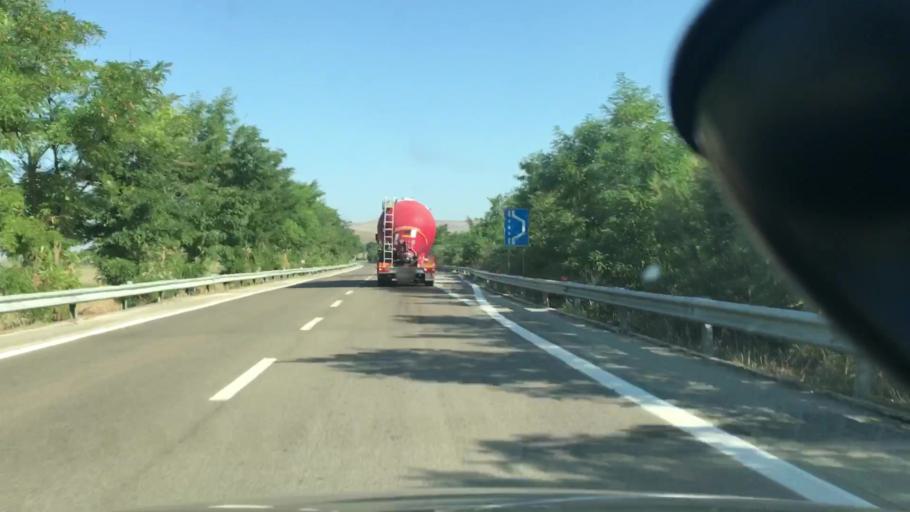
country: IT
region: Basilicate
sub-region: Provincia di Matera
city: Irsina
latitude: 40.8018
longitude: 16.2742
